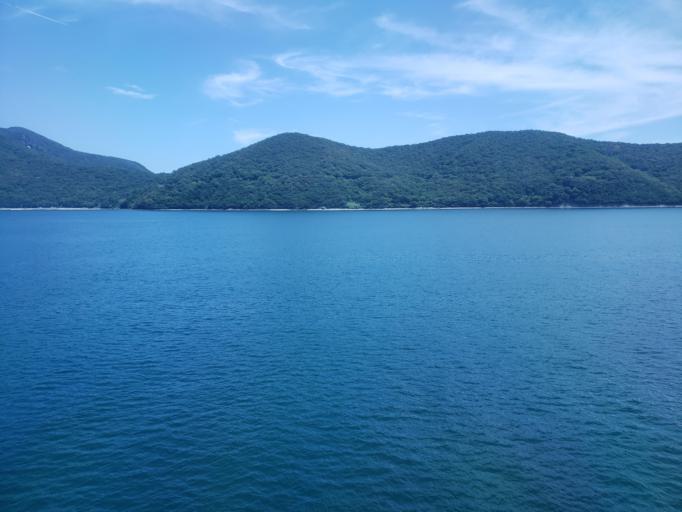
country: JP
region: Kagawa
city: Tonosho
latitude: 34.4346
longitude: 134.3223
